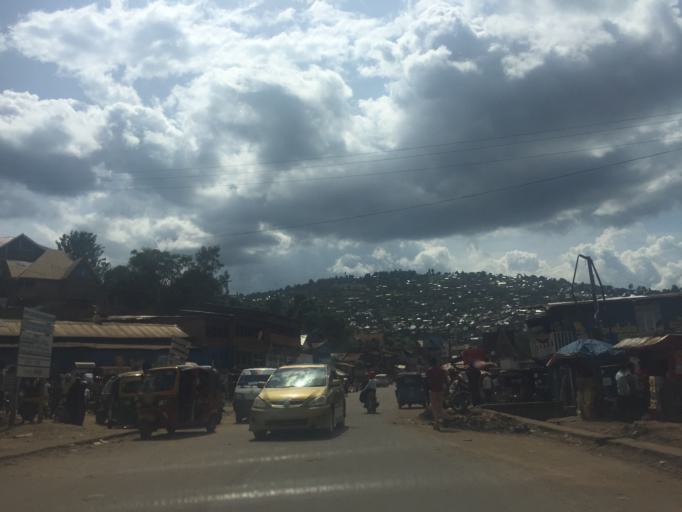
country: CD
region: South Kivu
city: Bukavu
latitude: -2.4839
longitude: 28.8428
